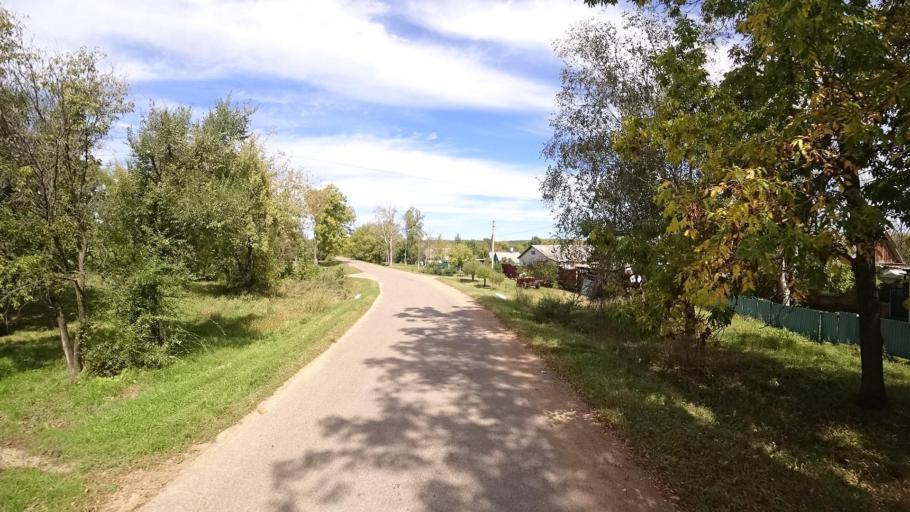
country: RU
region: Primorskiy
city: Yakovlevka
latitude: 44.6459
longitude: 133.5963
